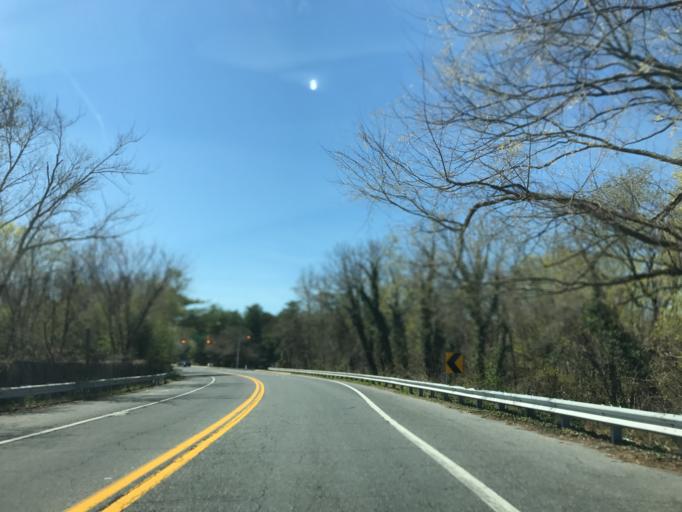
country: US
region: Maryland
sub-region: Anne Arundel County
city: Severn
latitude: 39.1344
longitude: -76.6985
